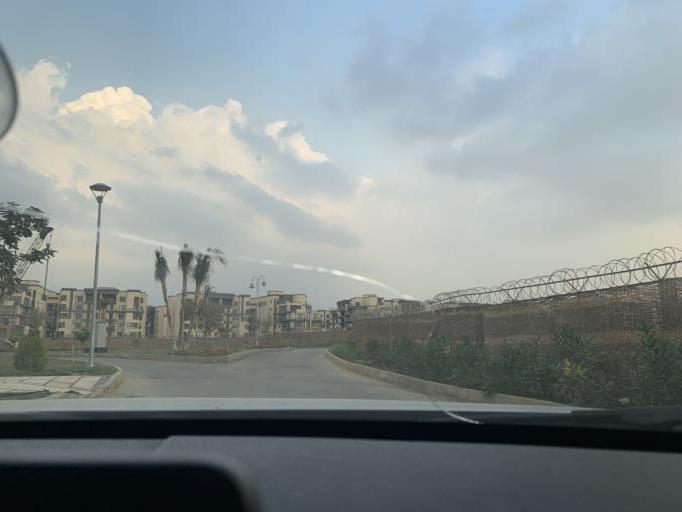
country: EG
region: Muhafazat al Qalyubiyah
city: Al Khankah
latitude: 30.0987
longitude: 31.6546
